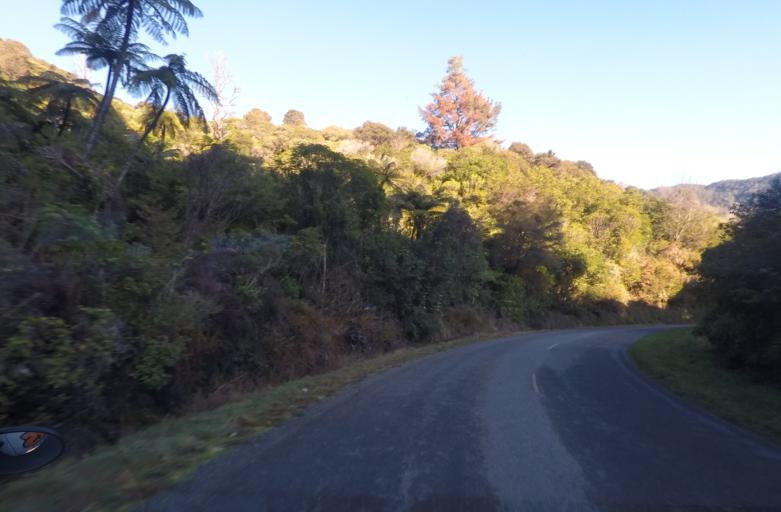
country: NZ
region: Marlborough
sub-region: Marlborough District
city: Picton
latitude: -41.2716
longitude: 173.9709
